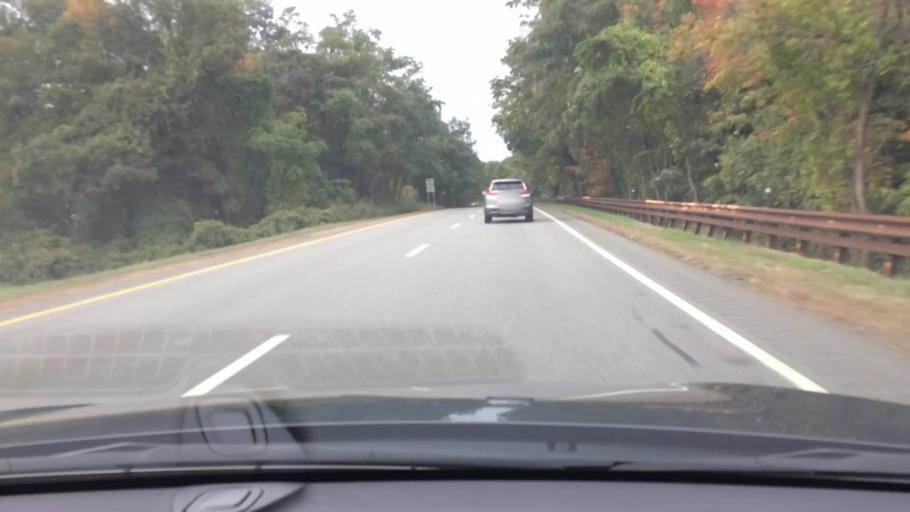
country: US
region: New Jersey
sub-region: Bergen County
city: Tenafly
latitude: 40.9132
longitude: -73.9345
